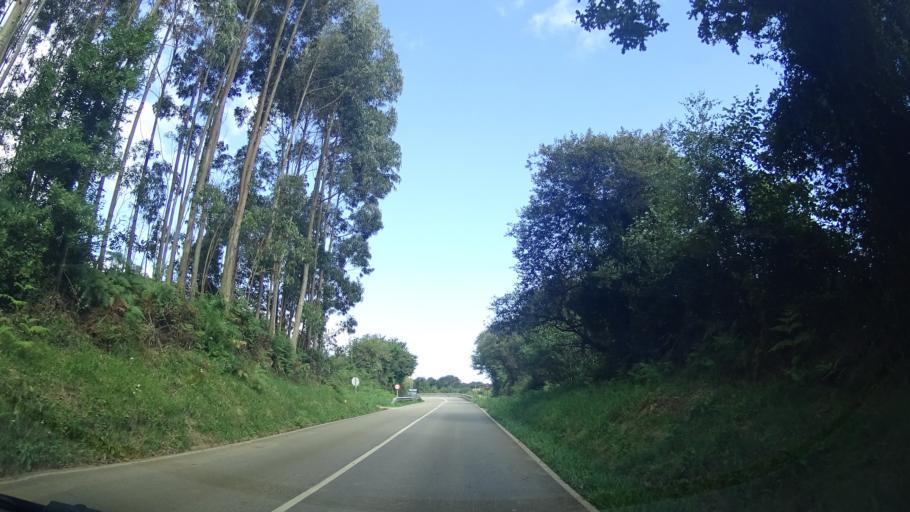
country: ES
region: Asturias
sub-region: Province of Asturias
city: Ribadesella
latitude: 43.4733
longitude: -5.1440
